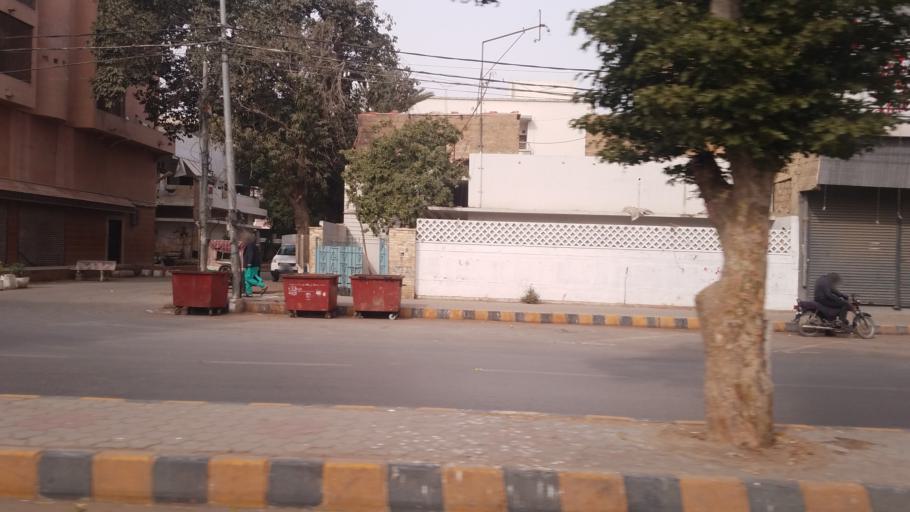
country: PK
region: Sindh
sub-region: Karachi District
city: Karachi
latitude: 24.8678
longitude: 67.0573
